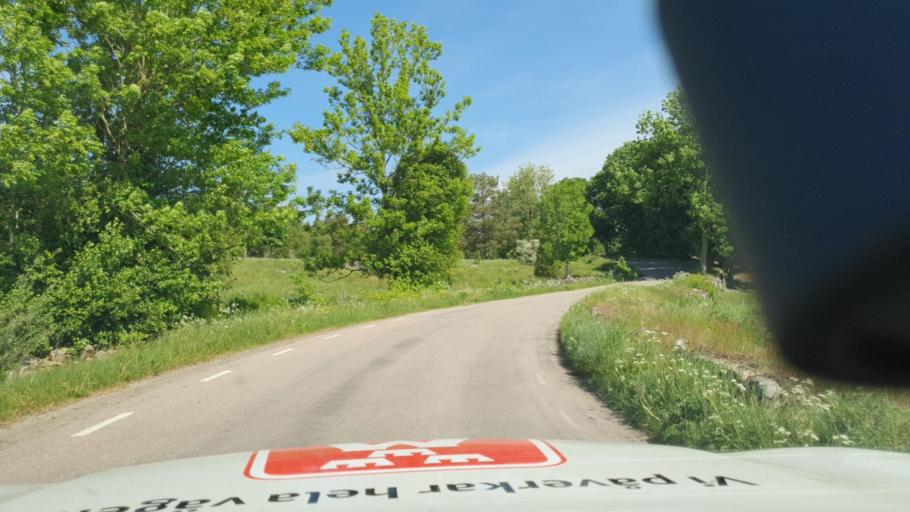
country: SE
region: Vaestra Goetaland
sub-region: Herrljunga Kommun
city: Herrljunga
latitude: 58.0054
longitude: 13.0880
